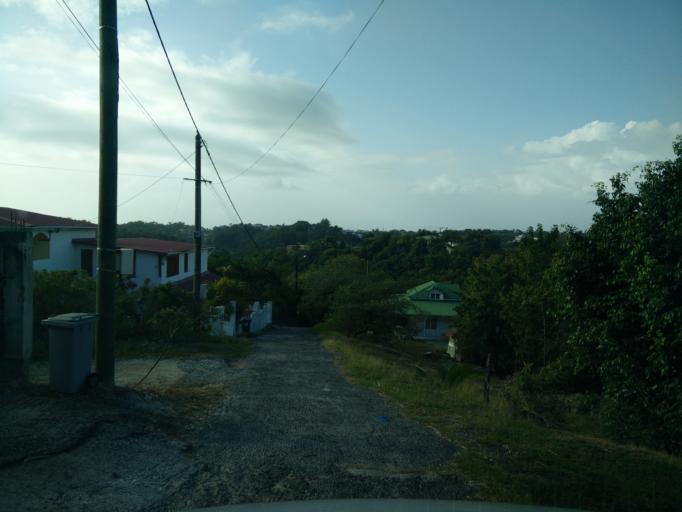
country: GP
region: Guadeloupe
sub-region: Guadeloupe
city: Le Gosier
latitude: 16.2284
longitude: -61.4578
